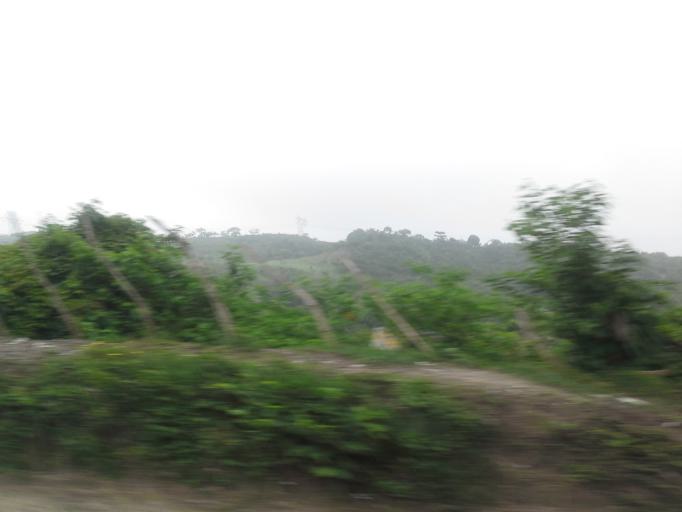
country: CO
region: Sucre
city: Ovejas
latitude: 9.5305
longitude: -75.2238
